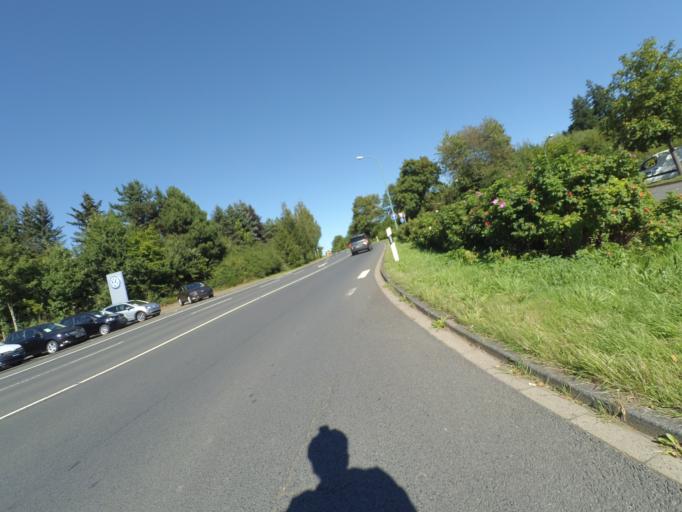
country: DE
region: Rheinland-Pfalz
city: Daun
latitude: 50.1970
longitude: 6.8168
